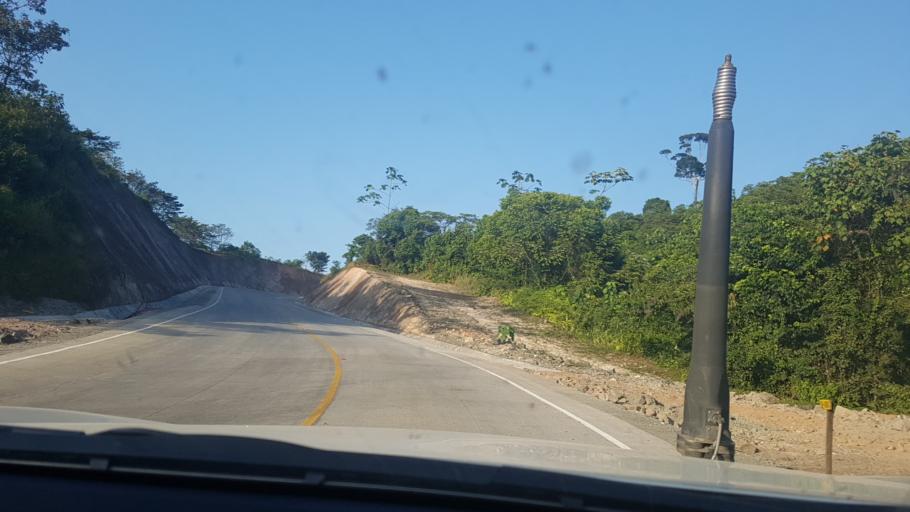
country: NI
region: Atlantico Sur
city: Rama
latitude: 11.8272
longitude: -84.0824
